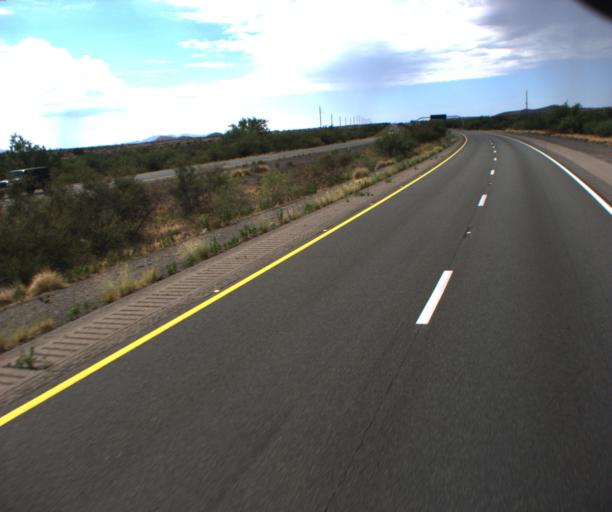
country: US
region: Arizona
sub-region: Yavapai County
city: Spring Valley
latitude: 34.3619
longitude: -112.1170
